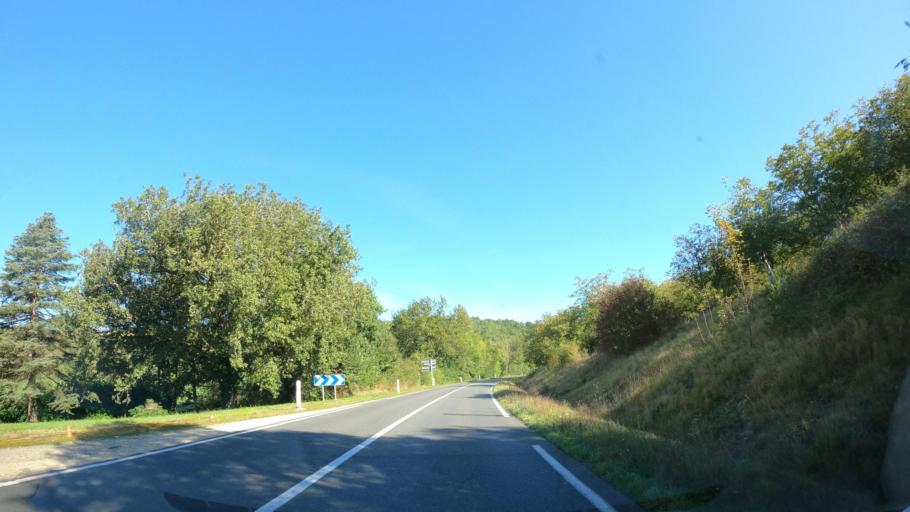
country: FR
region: Aquitaine
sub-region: Departement de la Dordogne
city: Vergt
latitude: 45.0556
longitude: 0.6542
